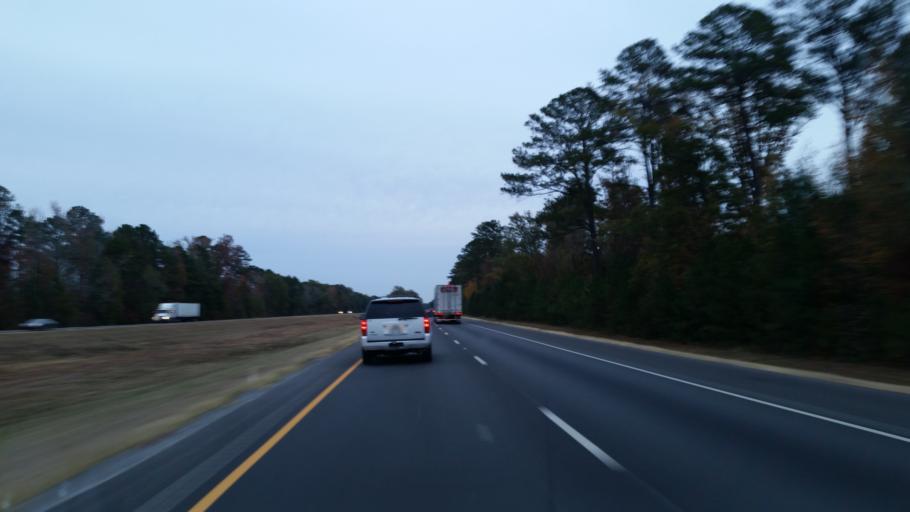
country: US
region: Alabama
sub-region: Greene County
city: Eutaw
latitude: 32.8131
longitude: -88.0063
